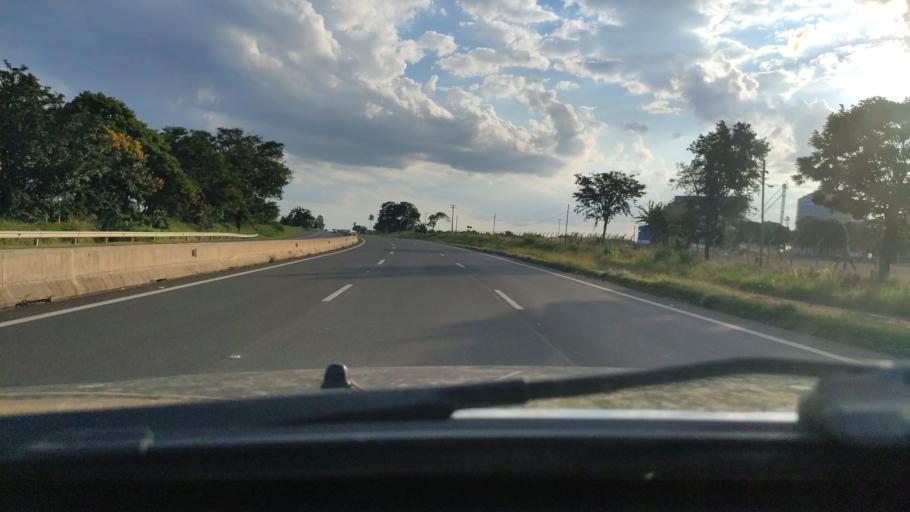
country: BR
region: Sao Paulo
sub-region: Mogi-Mirim
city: Mogi Mirim
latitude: -22.4513
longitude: -47.0853
